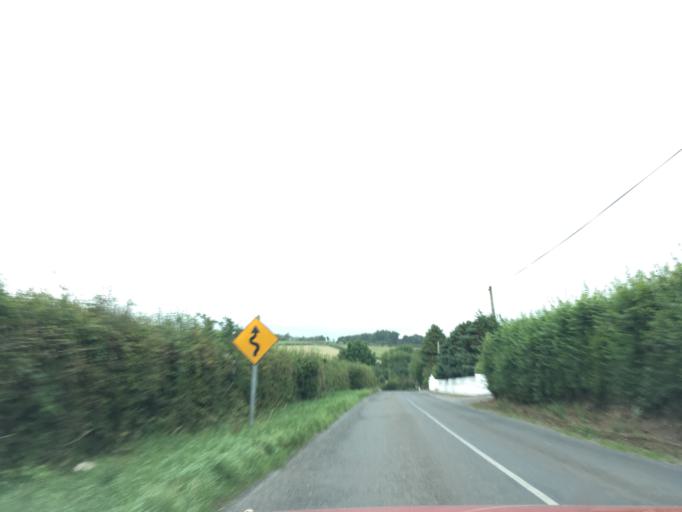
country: IE
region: Munster
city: Cashel
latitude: 52.4695
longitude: -7.8535
